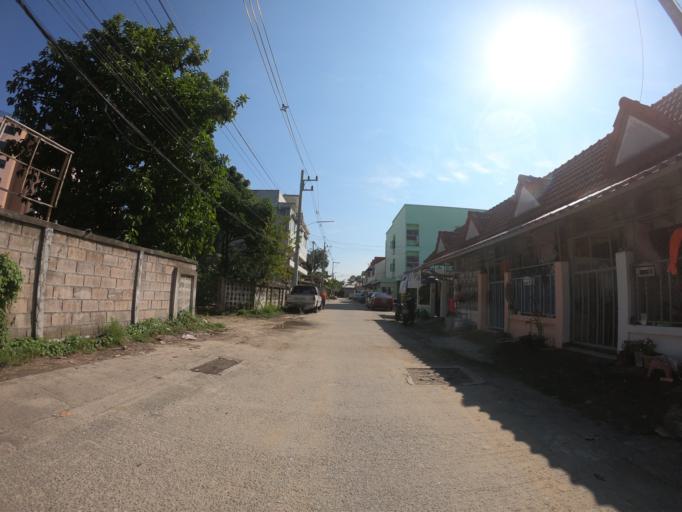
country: TH
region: Chiang Mai
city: Chiang Mai
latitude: 18.8029
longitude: 98.9925
